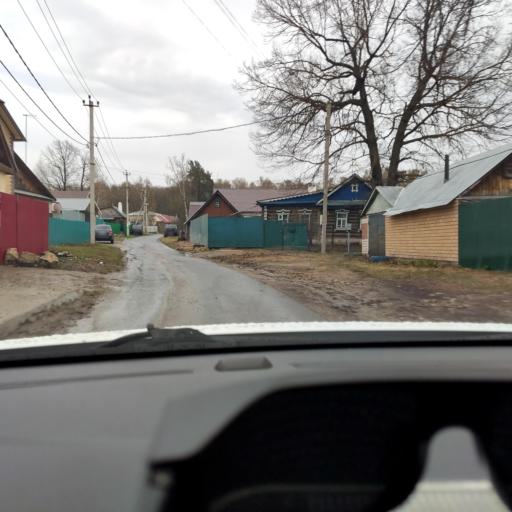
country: RU
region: Tatarstan
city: Vysokaya Gora
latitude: 55.9286
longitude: 49.3057
